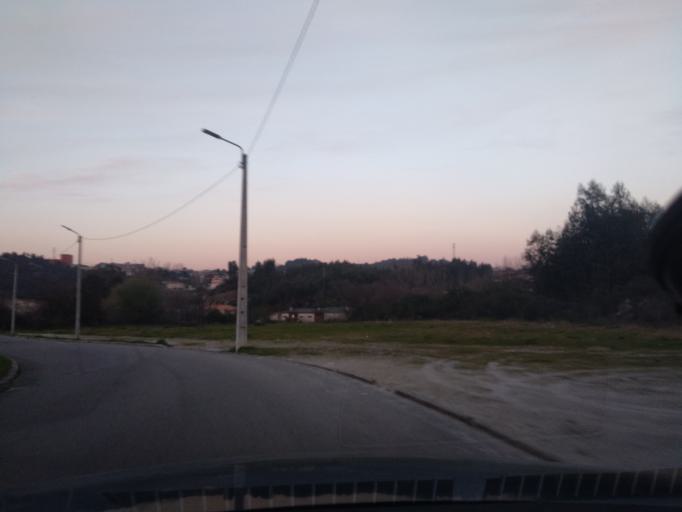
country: PT
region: Porto
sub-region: Paredes
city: Lordelo
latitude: 41.2347
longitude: -8.4137
